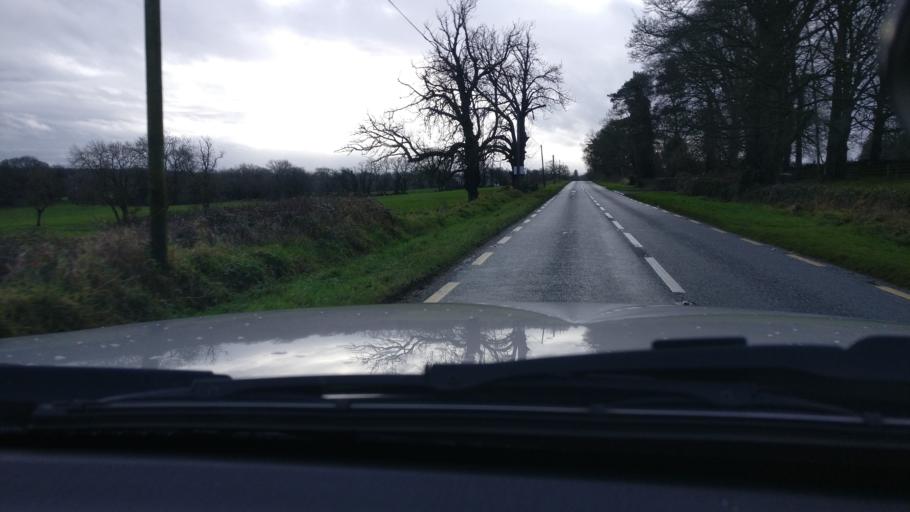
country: IE
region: Leinster
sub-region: An Iarmhi
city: Moate
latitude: 53.6276
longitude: -7.6946
